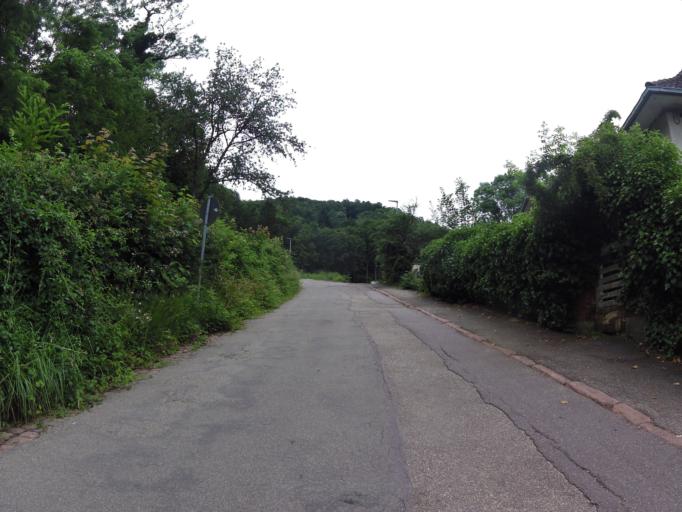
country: DE
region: Baden-Wuerttemberg
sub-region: Freiburg Region
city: Lahr
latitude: 48.3427
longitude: 7.8878
